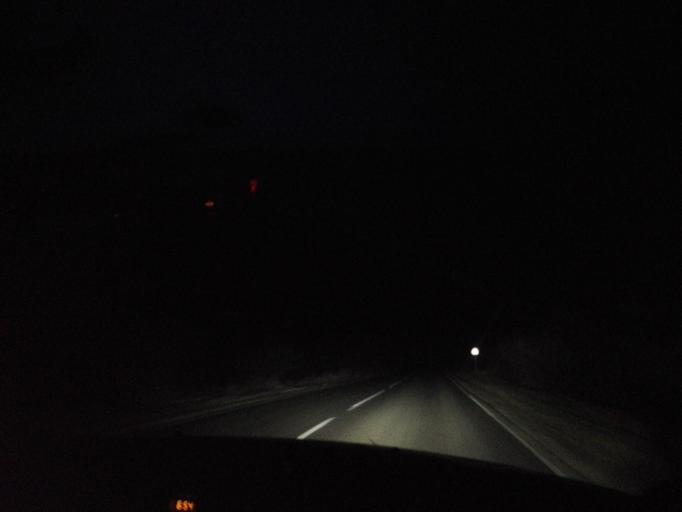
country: RU
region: Tula
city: Shvartsevskiy
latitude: 54.0774
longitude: 38.0001
